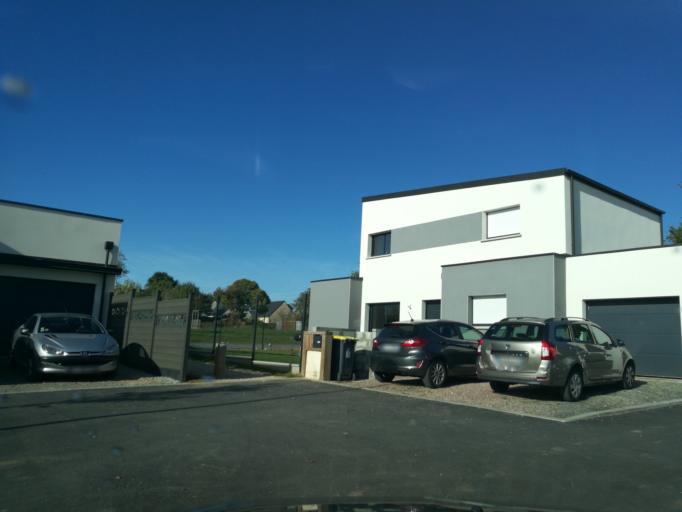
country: FR
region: Brittany
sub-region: Departement d'Ille-et-Vilaine
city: Pleumeleuc
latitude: 48.1831
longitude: -1.9132
